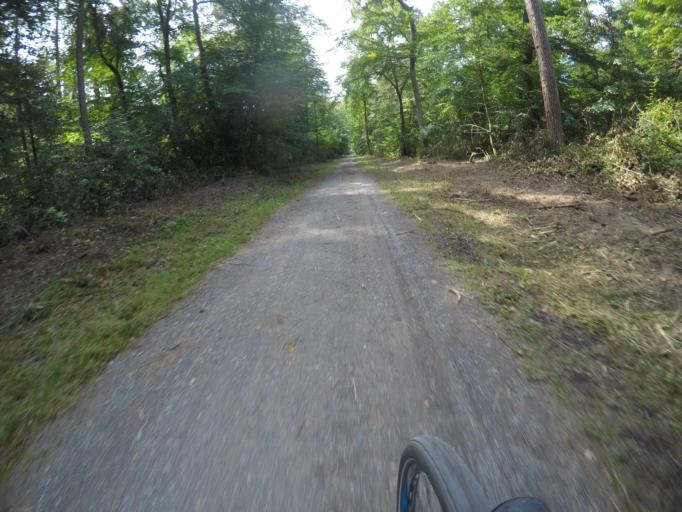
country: DE
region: Baden-Wuerttemberg
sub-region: Karlsruhe Region
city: Reilingen
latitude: 49.2780
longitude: 8.5687
